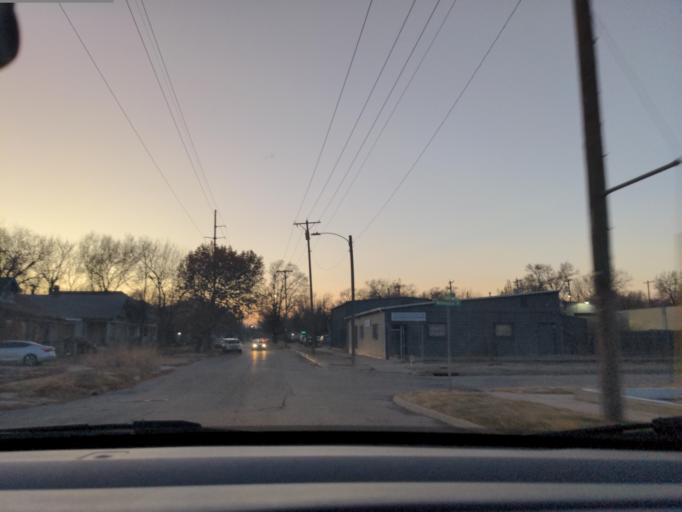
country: US
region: Kansas
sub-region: Sedgwick County
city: Wichita
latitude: 37.7045
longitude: -97.3391
